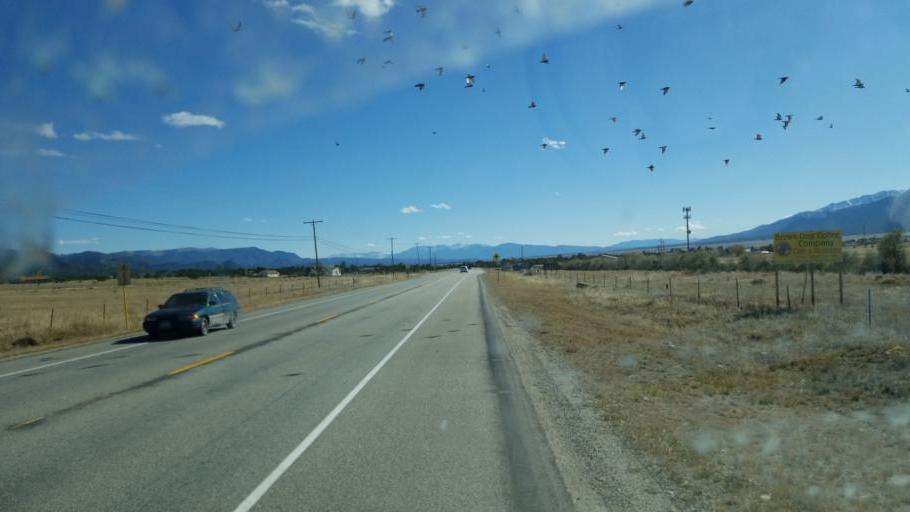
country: US
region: Colorado
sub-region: Chaffee County
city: Buena Vista
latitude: 38.8789
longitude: -106.1609
